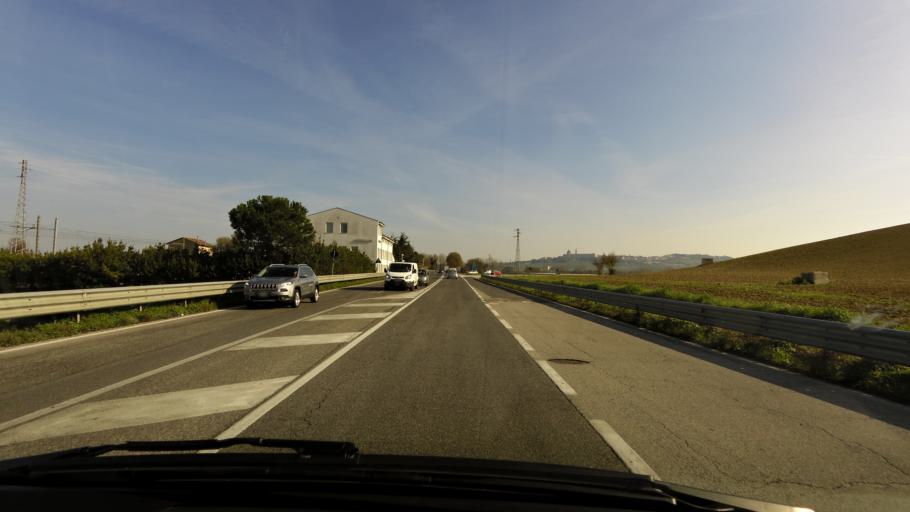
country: IT
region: The Marches
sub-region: Provincia di Ancona
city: Villa Musone
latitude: 43.4668
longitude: 13.6016
